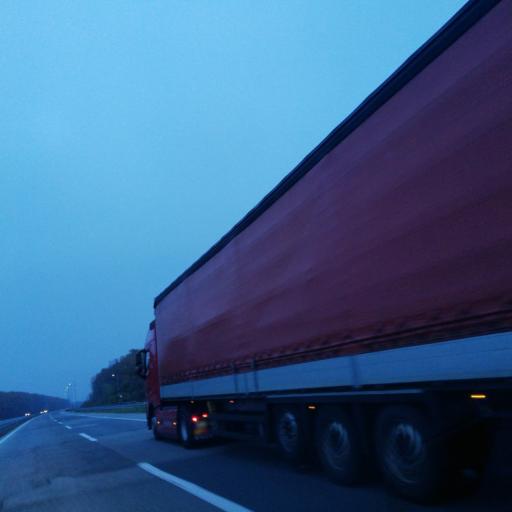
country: RS
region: Autonomna Pokrajina Vojvodina
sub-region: Sremski Okrug
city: Sid
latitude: 45.0472
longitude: 19.2261
